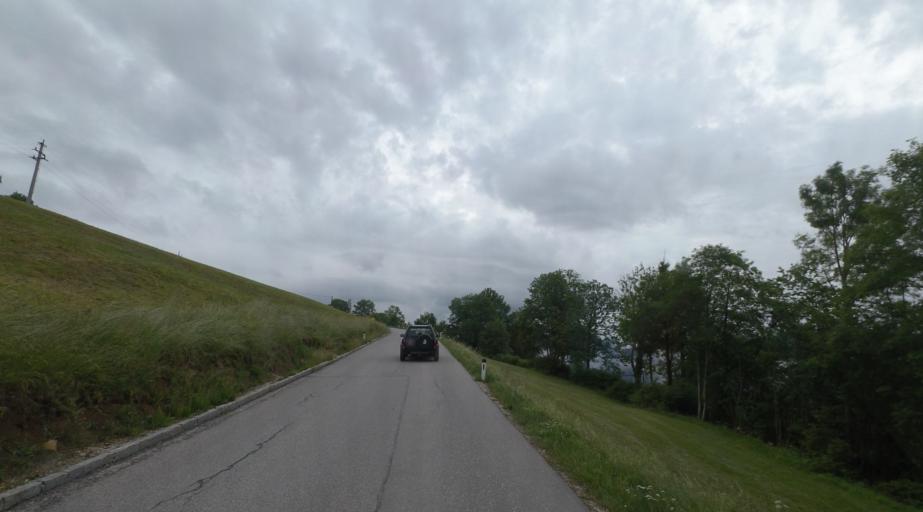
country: AT
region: Upper Austria
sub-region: Politischer Bezirk Kirchdorf an der Krems
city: Micheldorf in Oberoesterreich
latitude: 47.9218
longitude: 14.1591
